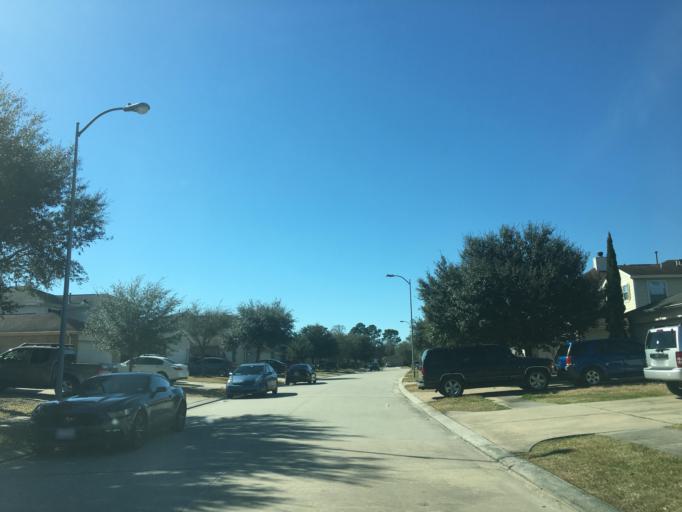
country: US
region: Texas
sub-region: Harris County
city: Spring
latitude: 30.0844
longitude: -95.4623
